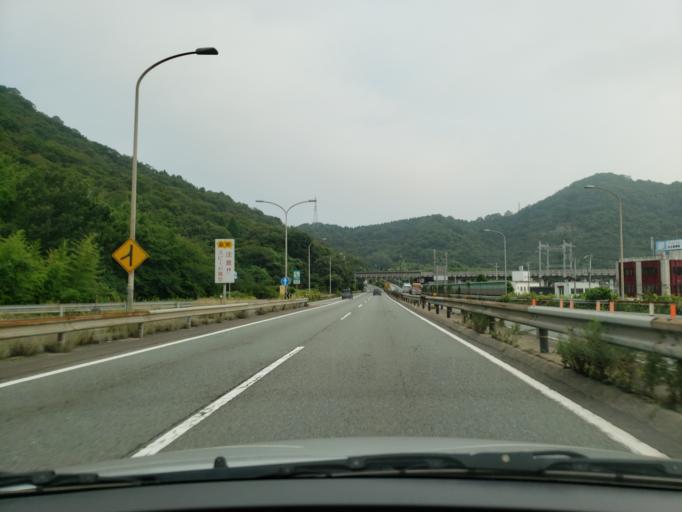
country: JP
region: Hyogo
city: Himeji
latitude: 34.8293
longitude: 134.6332
